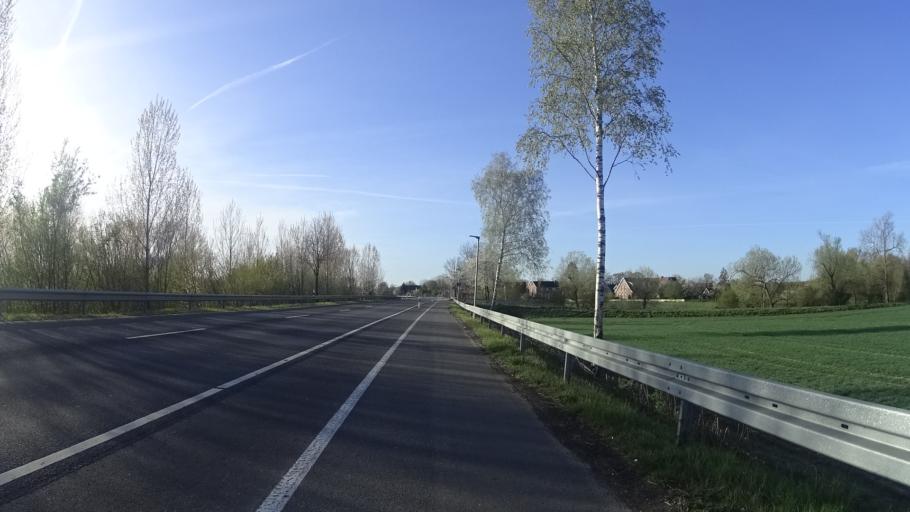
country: DE
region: North Rhine-Westphalia
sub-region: Regierungsbezirk Munster
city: Greven
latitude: 52.1080
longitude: 7.5837
